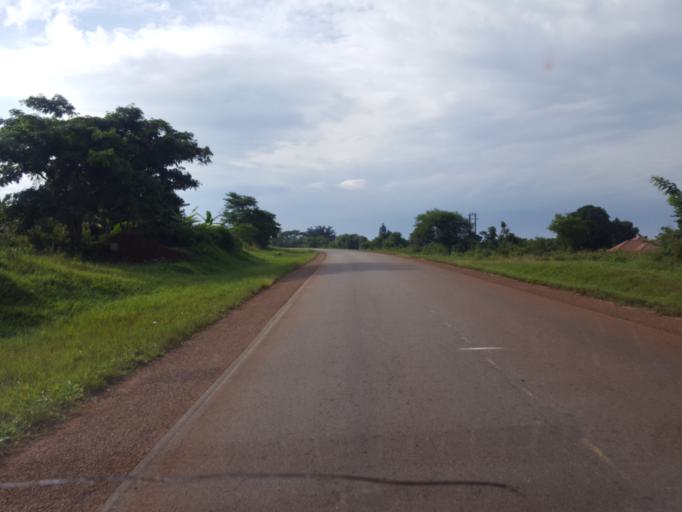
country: UG
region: Western Region
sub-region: Hoima District
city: Hoima
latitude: 1.2565
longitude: 31.5117
